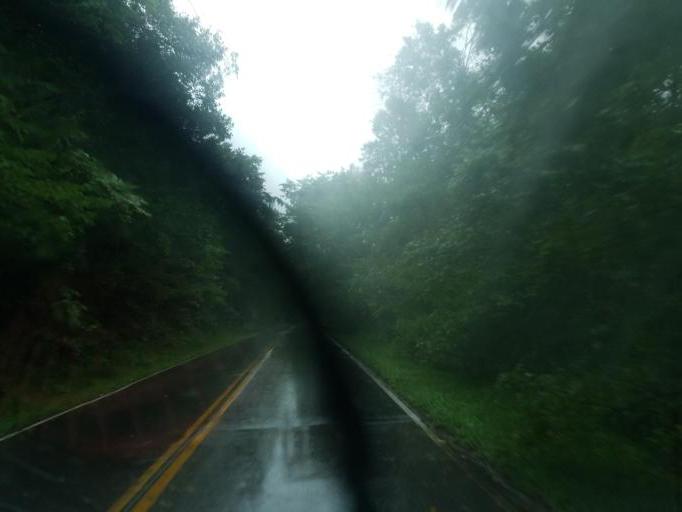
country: US
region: Kentucky
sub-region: Greenup County
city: Greenup
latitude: 38.5024
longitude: -82.9700
